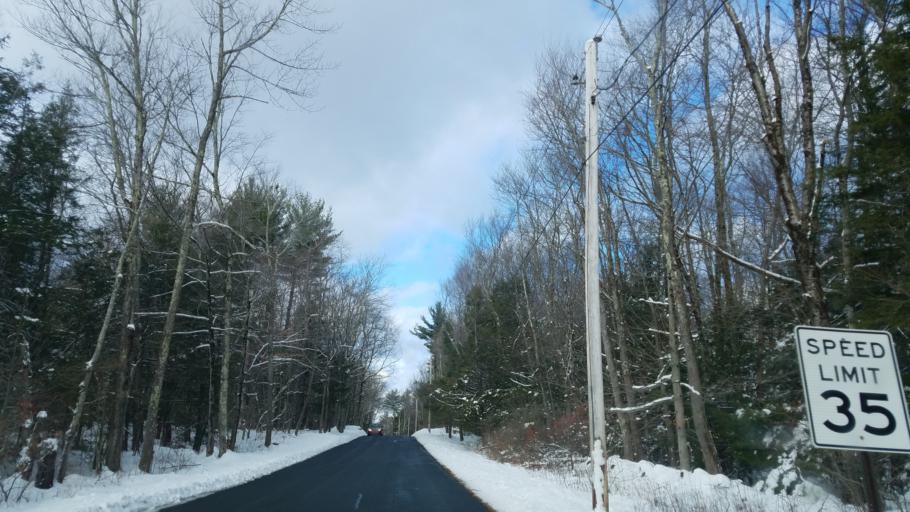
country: US
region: Connecticut
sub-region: Litchfield County
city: Winsted
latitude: 41.9841
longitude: -73.0874
